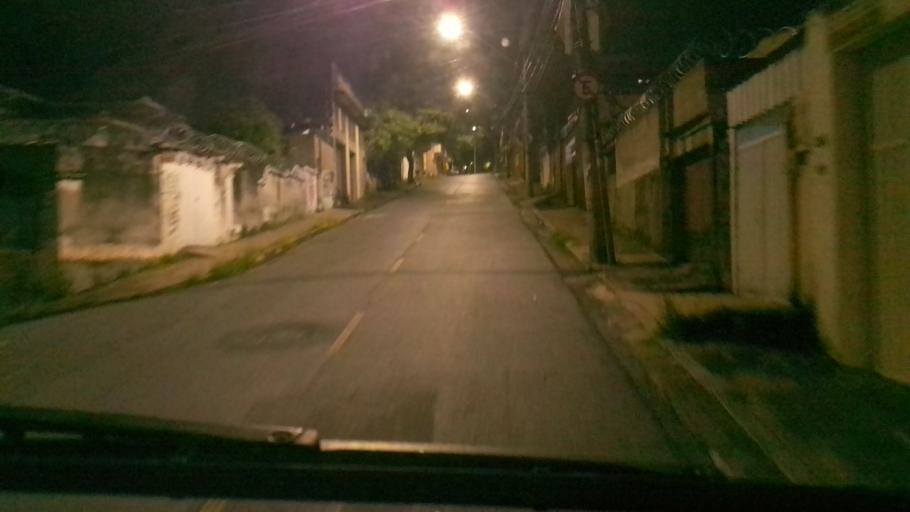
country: BR
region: Minas Gerais
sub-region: Belo Horizonte
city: Belo Horizonte
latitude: -19.9078
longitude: -43.9495
